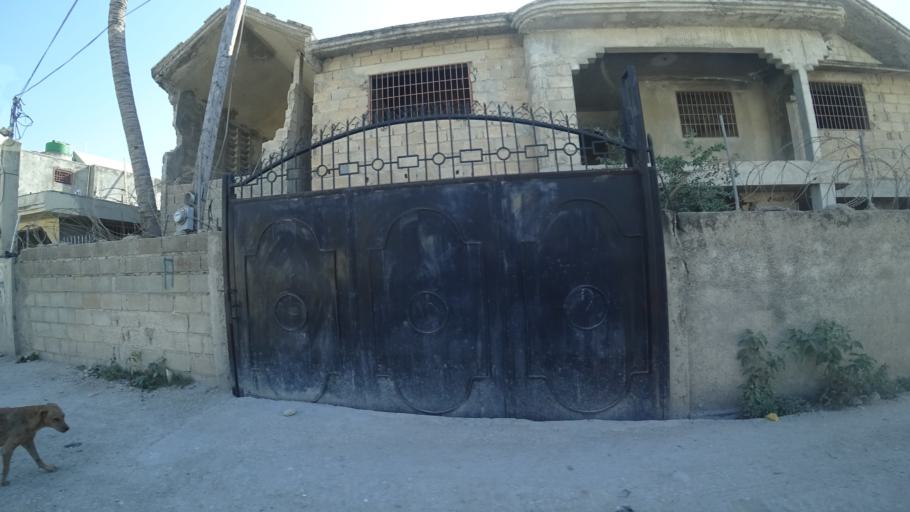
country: HT
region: Ouest
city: Delmas 73
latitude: 18.5568
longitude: -72.2841
